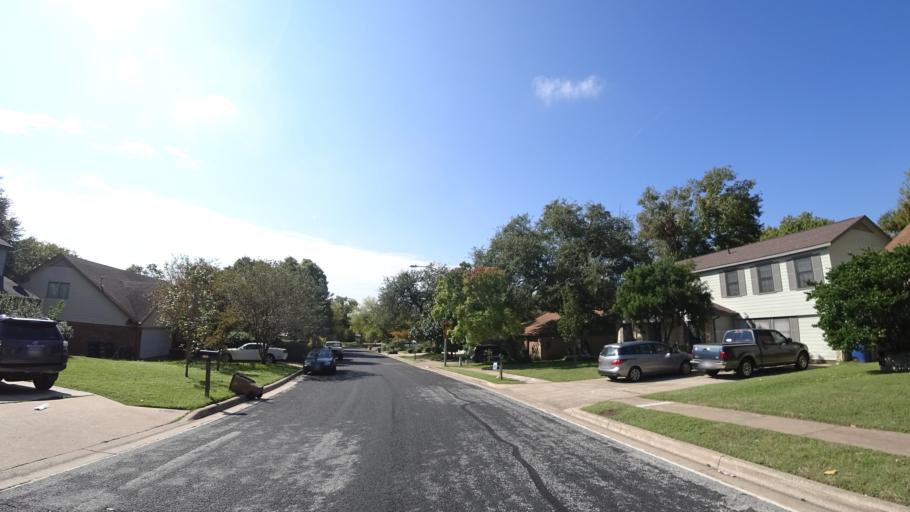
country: US
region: Texas
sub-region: Travis County
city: Shady Hollow
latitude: 30.1967
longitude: -97.8170
